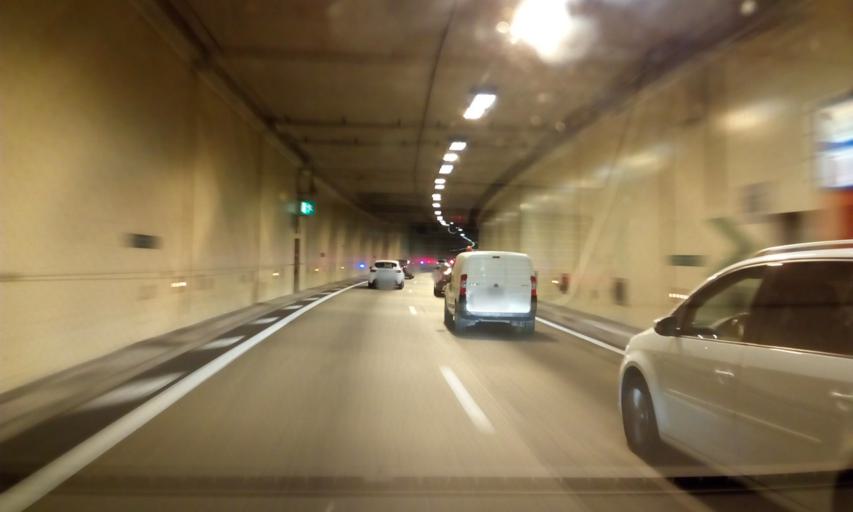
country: FR
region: Provence-Alpes-Cote d'Azur
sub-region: Departement du Var
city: Toulon
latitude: 43.1270
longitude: 5.9188
